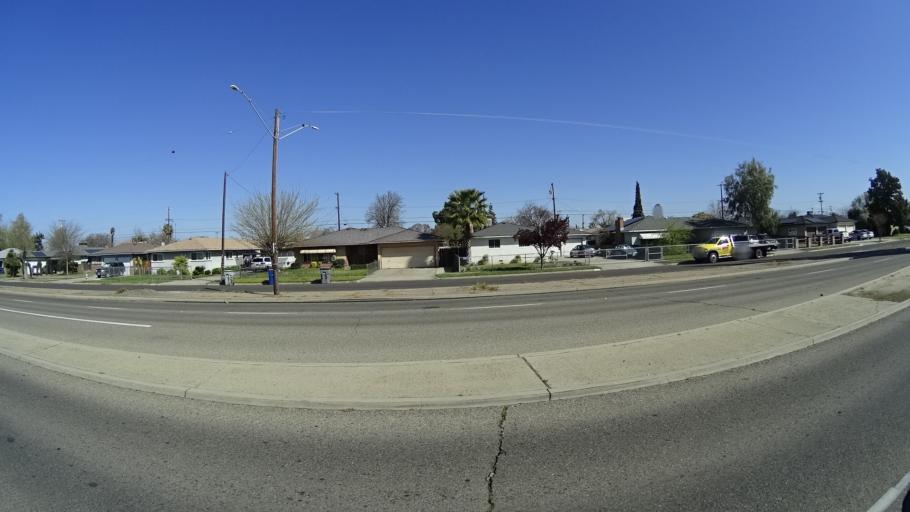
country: US
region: California
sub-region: Fresno County
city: Fresno
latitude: 36.7797
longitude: -119.7586
